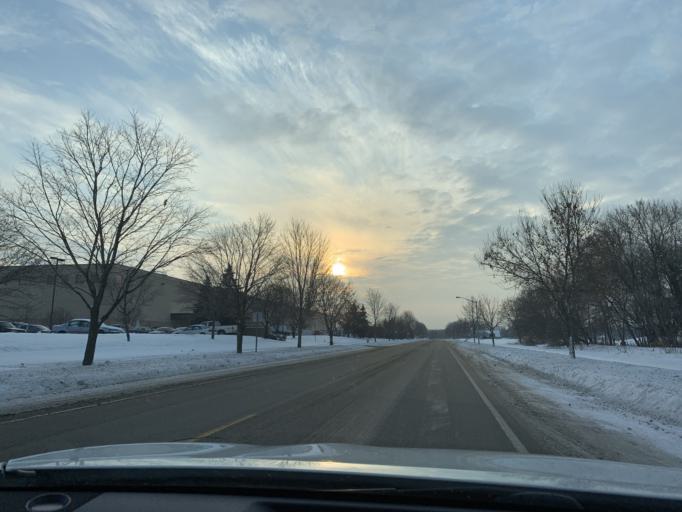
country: US
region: Minnesota
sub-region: Anoka County
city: Coon Rapids
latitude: 45.1577
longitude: -93.2836
